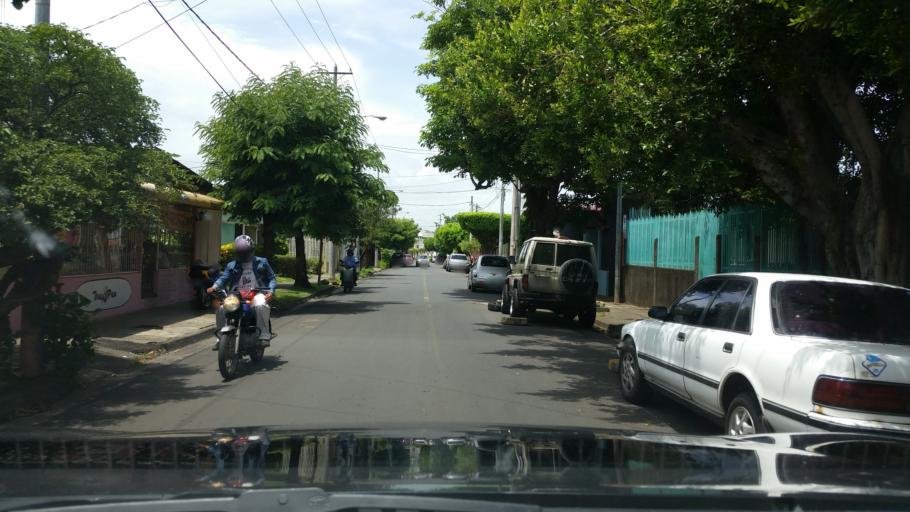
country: NI
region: Managua
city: Managua
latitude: 12.1237
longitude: -86.2520
